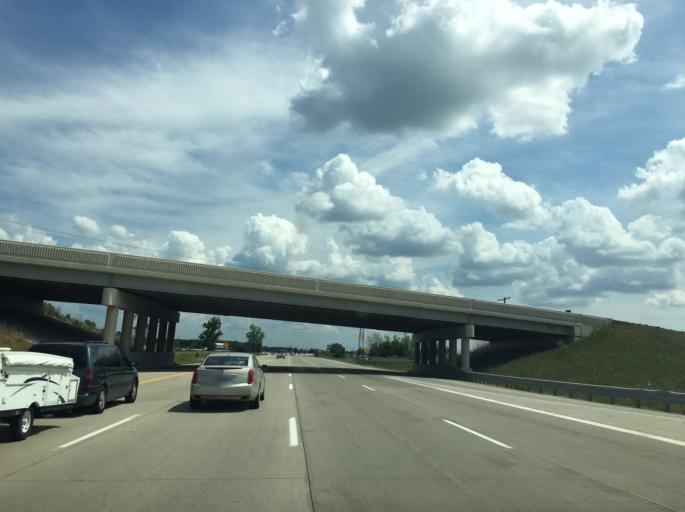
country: US
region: Michigan
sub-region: Bay County
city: Bay City
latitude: 43.5599
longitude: -83.9487
